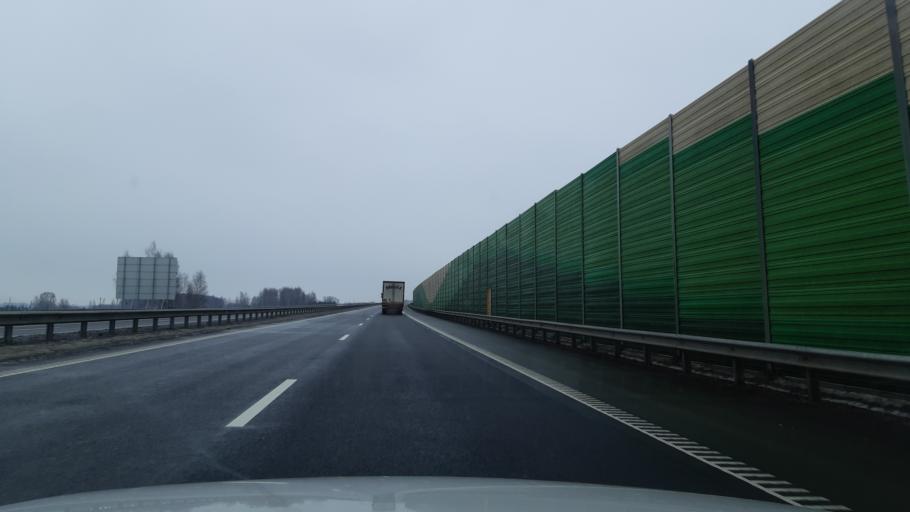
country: LT
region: Marijampoles apskritis
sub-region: Marijampole Municipality
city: Marijampole
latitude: 54.6201
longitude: 23.4176
